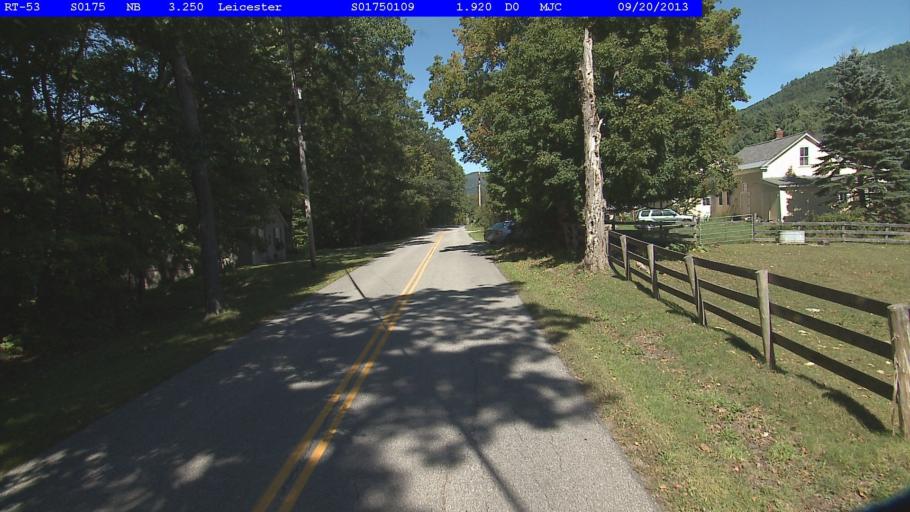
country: US
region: Vermont
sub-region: Rutland County
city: Brandon
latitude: 43.8705
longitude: -73.0648
